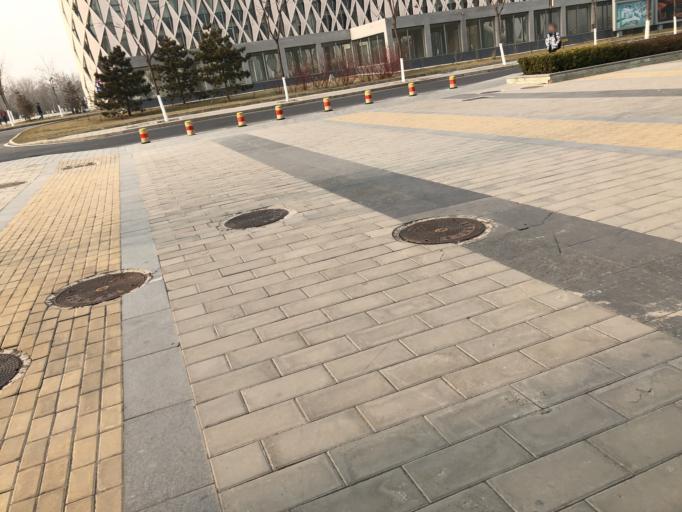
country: CN
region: Beijing
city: Daxing
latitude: 39.7444
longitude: 116.2826
